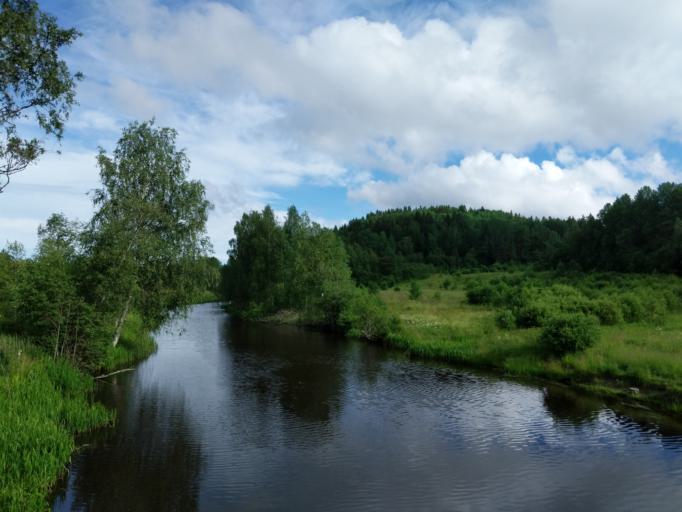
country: RU
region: Republic of Karelia
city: Khelyulya
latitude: 61.6359
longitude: 30.6044
